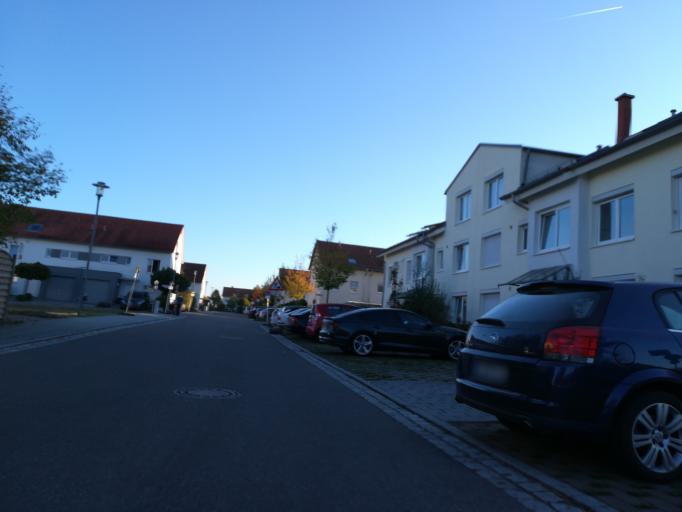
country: DE
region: Baden-Wuerttemberg
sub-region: Regierungsbezirk Stuttgart
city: Filderstadt
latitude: 48.6524
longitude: 9.1902
